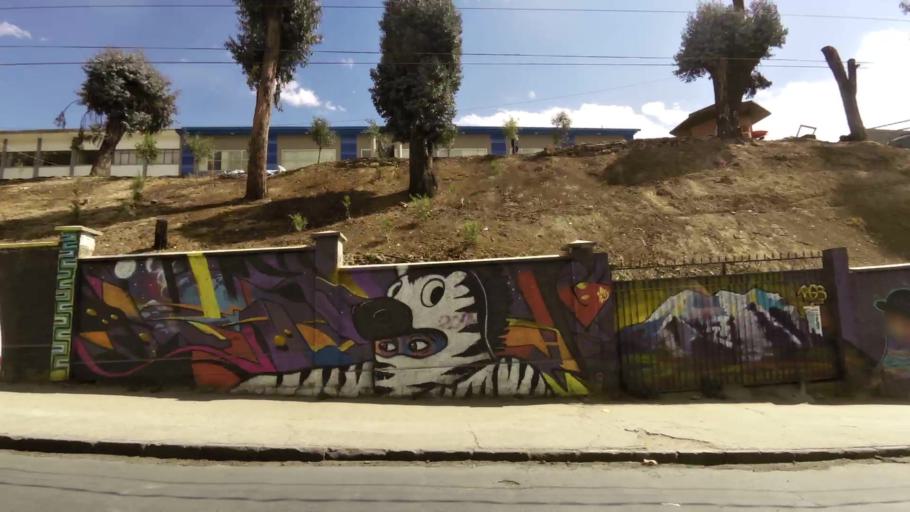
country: BO
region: La Paz
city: La Paz
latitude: -16.4899
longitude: -68.1446
